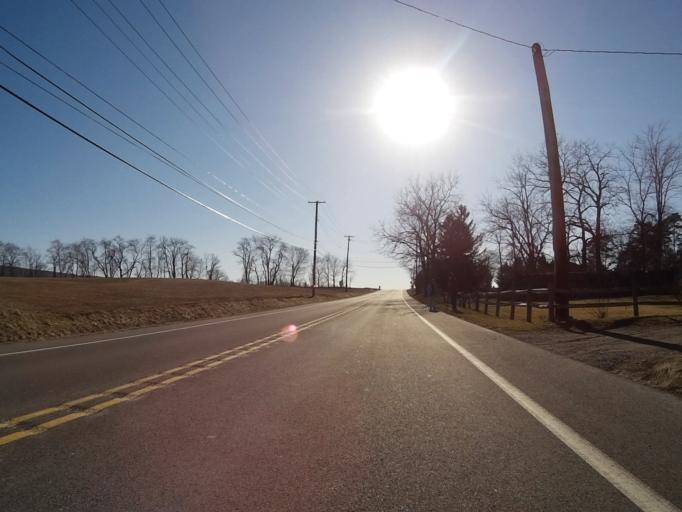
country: US
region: Pennsylvania
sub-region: Centre County
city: Pine Grove Mills
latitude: 40.7523
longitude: -77.8909
